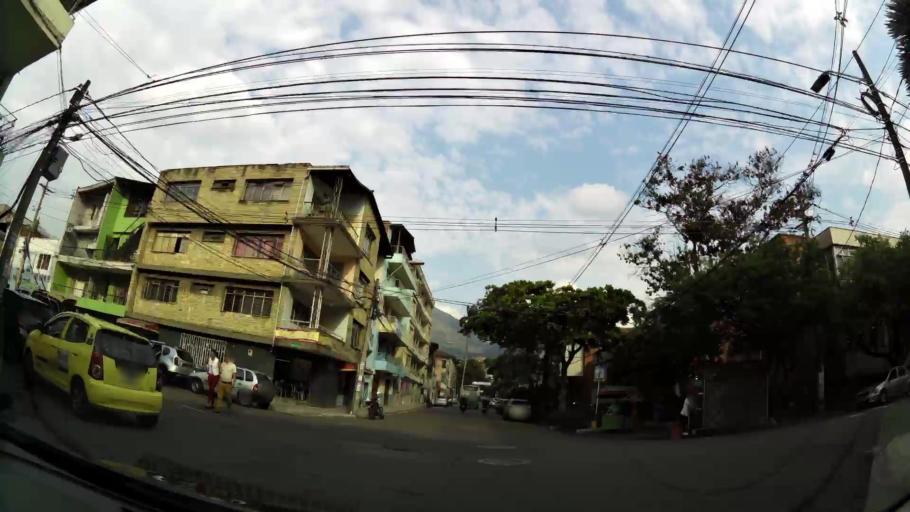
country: CO
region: Antioquia
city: Medellin
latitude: 6.2621
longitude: -75.5679
